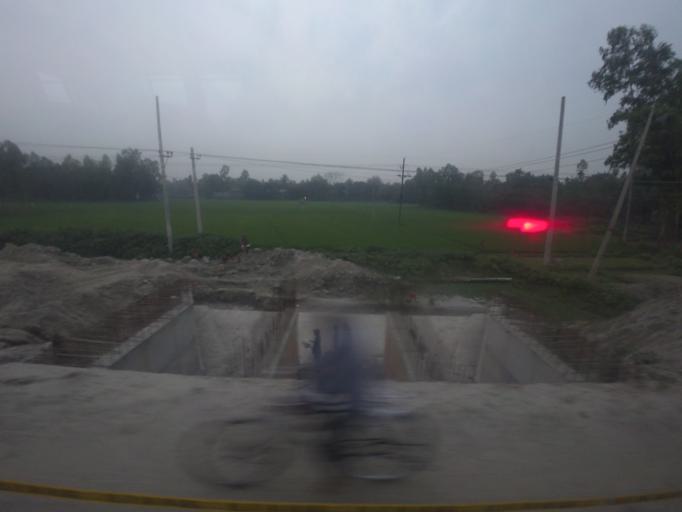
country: BD
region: Dhaka
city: Tangail
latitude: 24.3260
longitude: 89.9247
